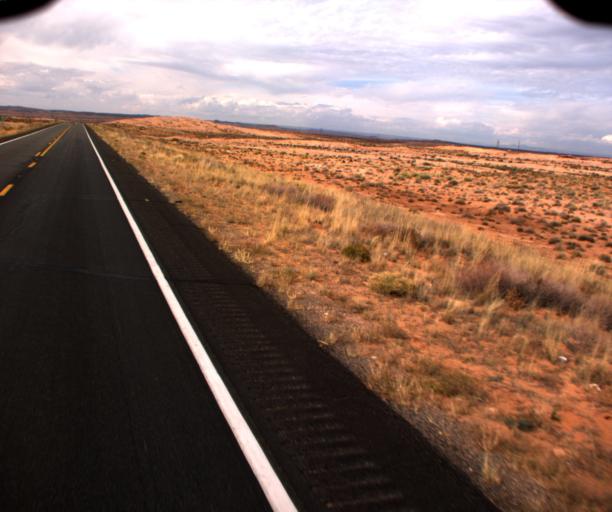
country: US
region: Arizona
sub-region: Apache County
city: Many Farms
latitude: 36.9315
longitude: -109.6261
